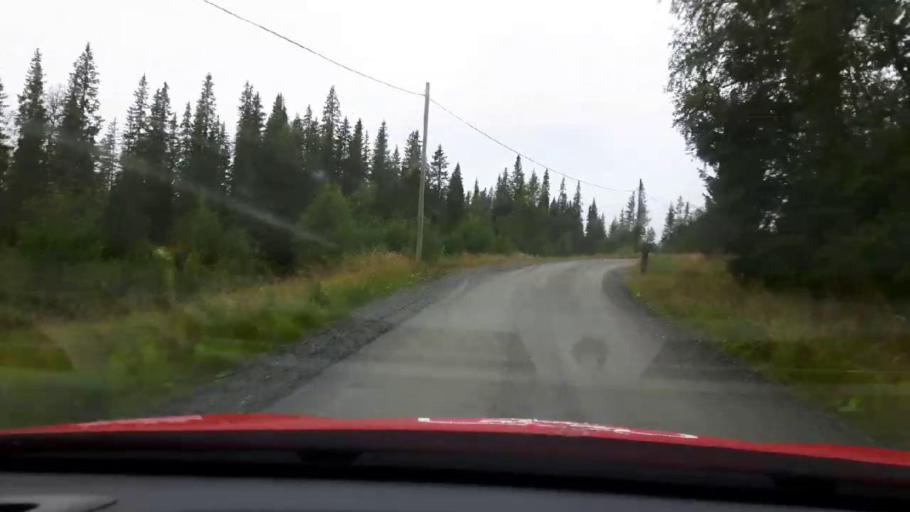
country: SE
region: Jaemtland
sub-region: Are Kommun
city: Are
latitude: 63.5011
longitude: 12.7548
